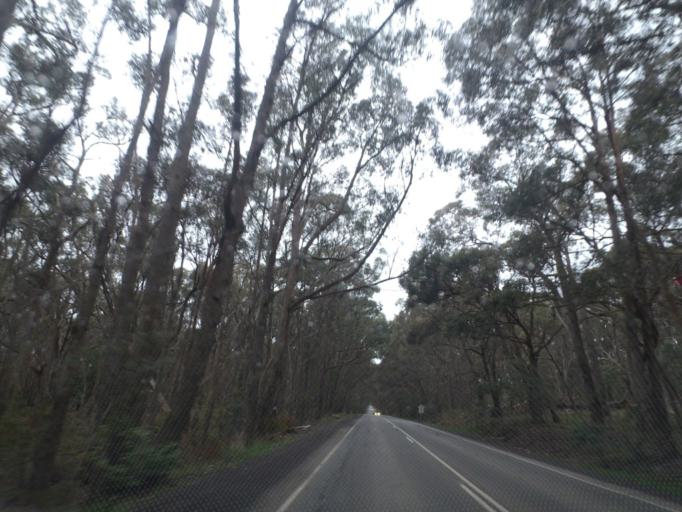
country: AU
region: Victoria
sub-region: Hume
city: Sunbury
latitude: -37.3454
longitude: 144.6672
